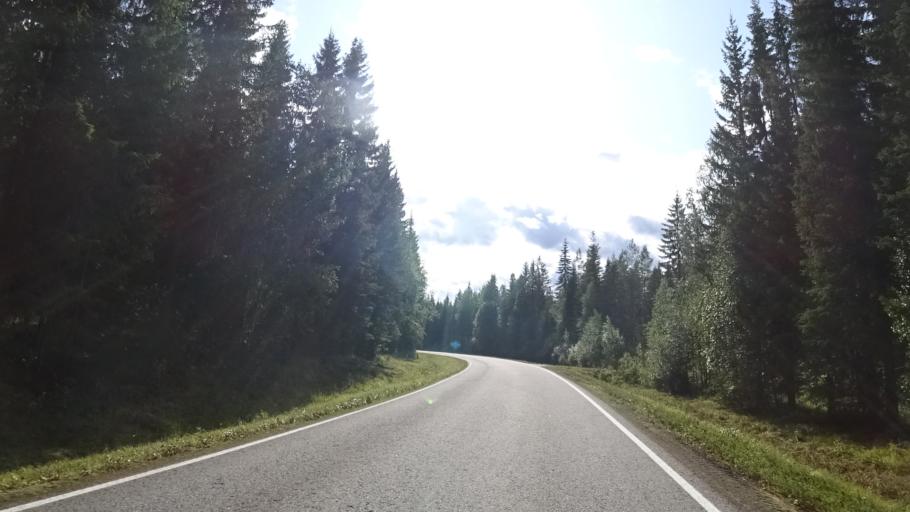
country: RU
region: Republic of Karelia
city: Vyartsilya
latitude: 62.2434
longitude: 30.7091
